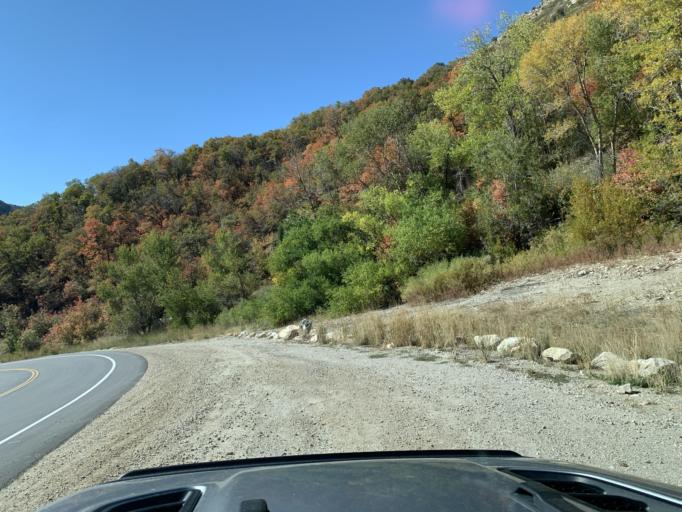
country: US
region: Utah
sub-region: Weber County
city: Liberty
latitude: 41.3179
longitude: -111.9088
